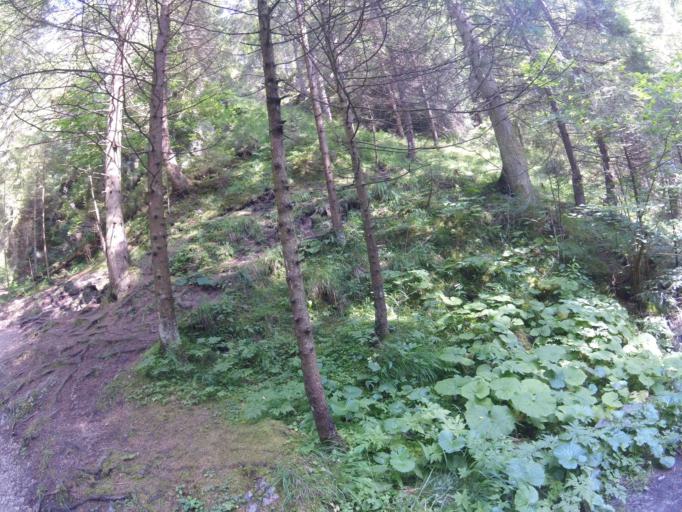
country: SK
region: Zilinsky
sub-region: Okres Zilina
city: Terchova
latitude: 49.2503
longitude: 19.0763
